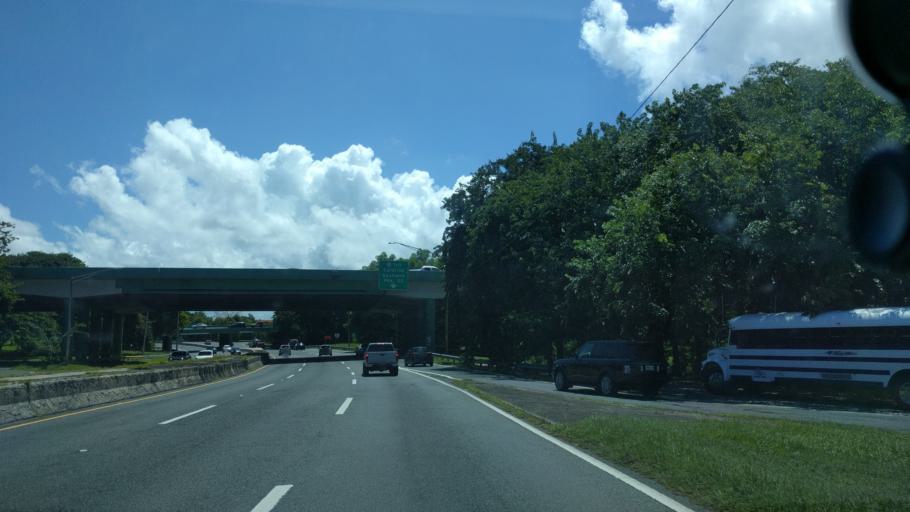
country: PR
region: San Juan
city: San Juan
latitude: 18.4407
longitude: -66.0724
